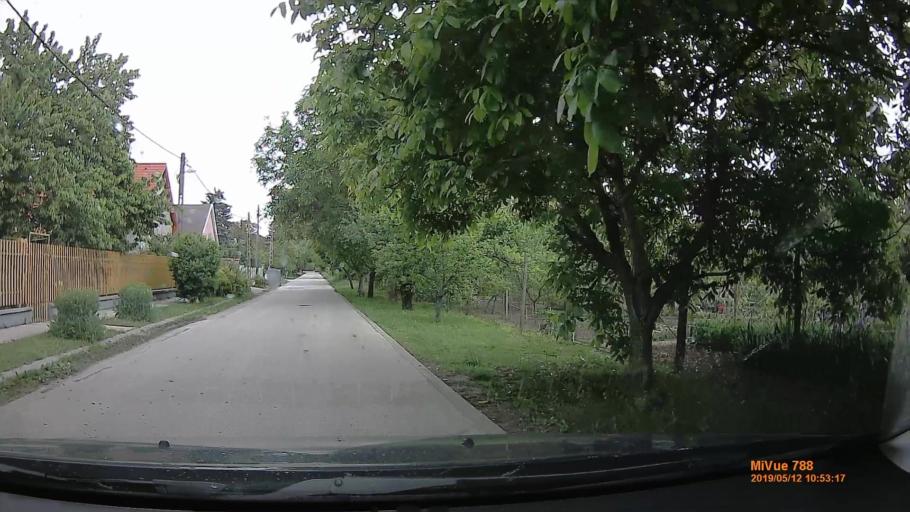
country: HU
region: Budapest
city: Budapest XVII. keruelet
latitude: 47.4771
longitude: 19.2206
